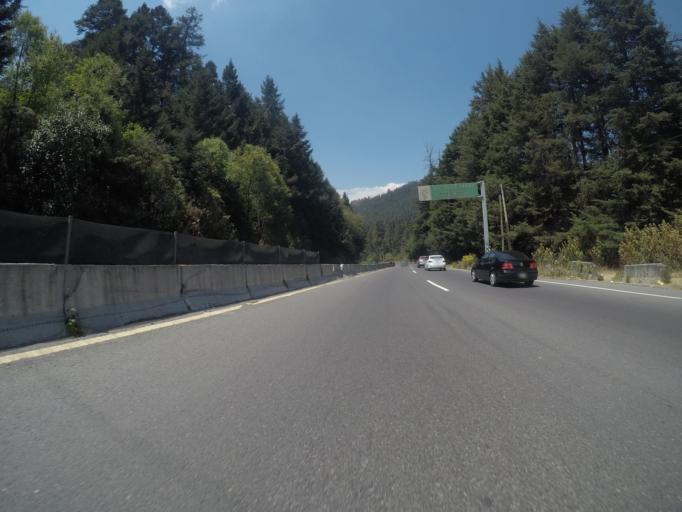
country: MX
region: Mexico City
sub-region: Cuajimalpa de Morelos
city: San Lorenzo Acopilco
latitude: 19.2941
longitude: -99.3550
